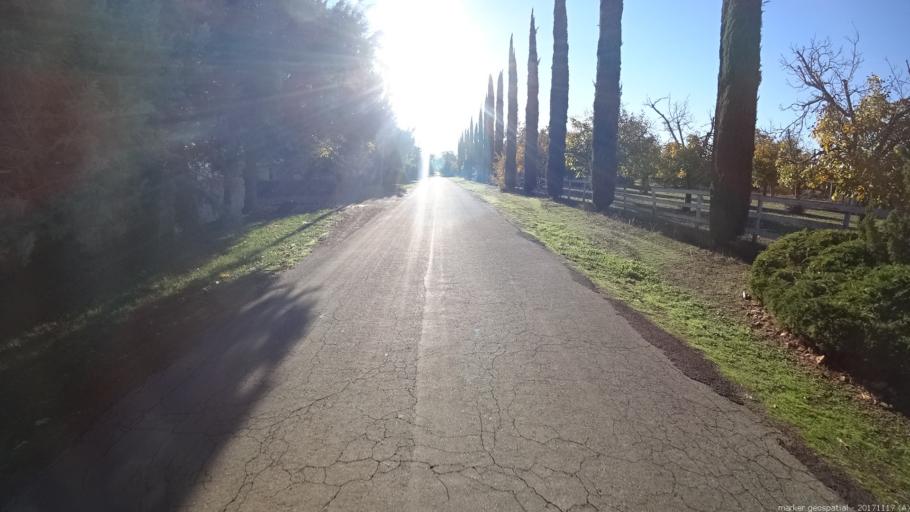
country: US
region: California
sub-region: Shasta County
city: Cottonwood
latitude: 40.4256
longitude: -122.2254
